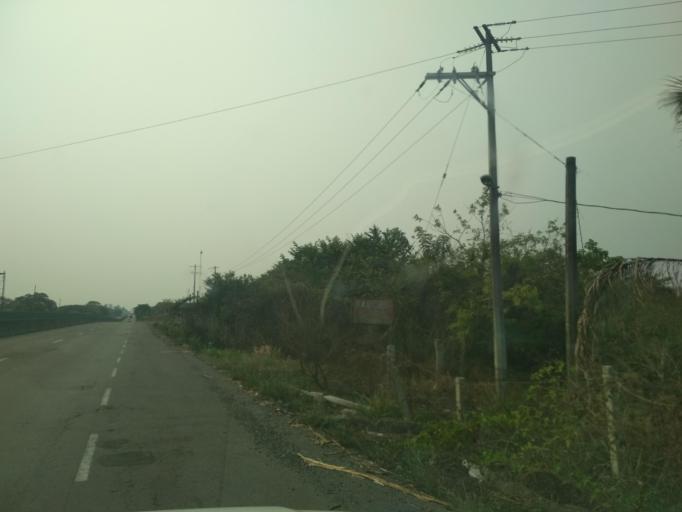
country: MX
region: Veracruz
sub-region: Veracruz
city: Las Amapolas
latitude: 19.1267
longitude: -96.2430
